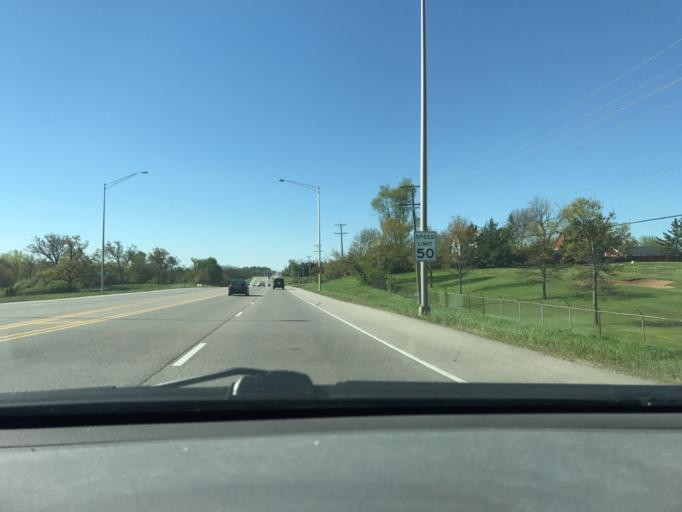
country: US
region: Illinois
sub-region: Kane County
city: Sleepy Hollow
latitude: 42.1175
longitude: -88.3352
